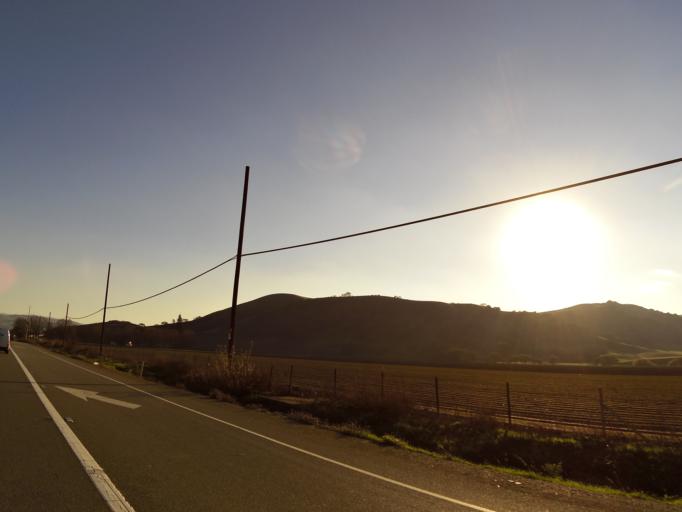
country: US
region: California
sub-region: Santa Clara County
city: Gilroy
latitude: 36.9684
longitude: -121.5533
